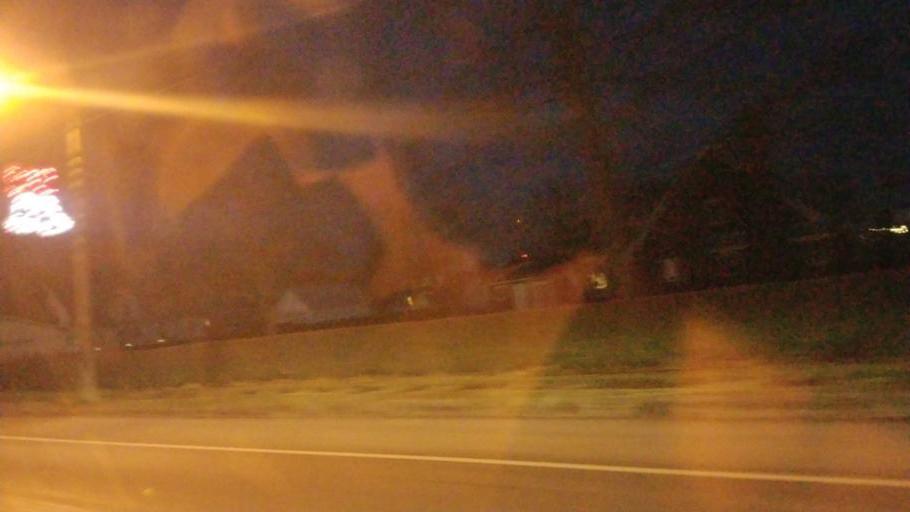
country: US
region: Indiana
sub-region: Adams County
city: Berne
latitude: 40.6597
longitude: -84.9556
